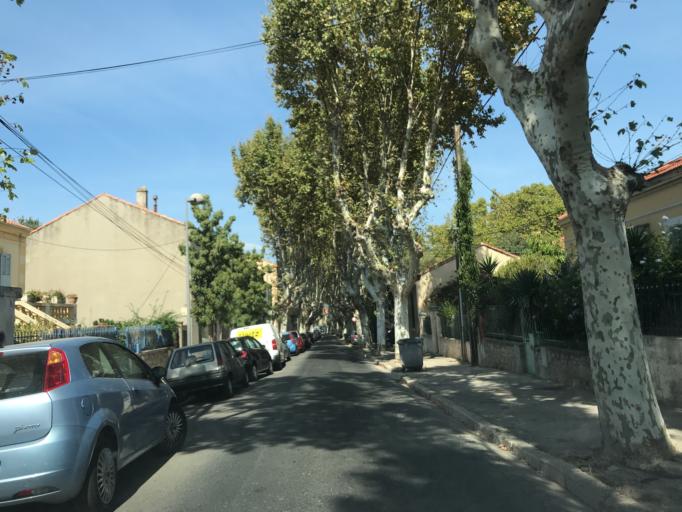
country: FR
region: Provence-Alpes-Cote d'Azur
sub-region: Departement du Var
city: La Seyne-sur-Mer
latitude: 43.0957
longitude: 5.8841
